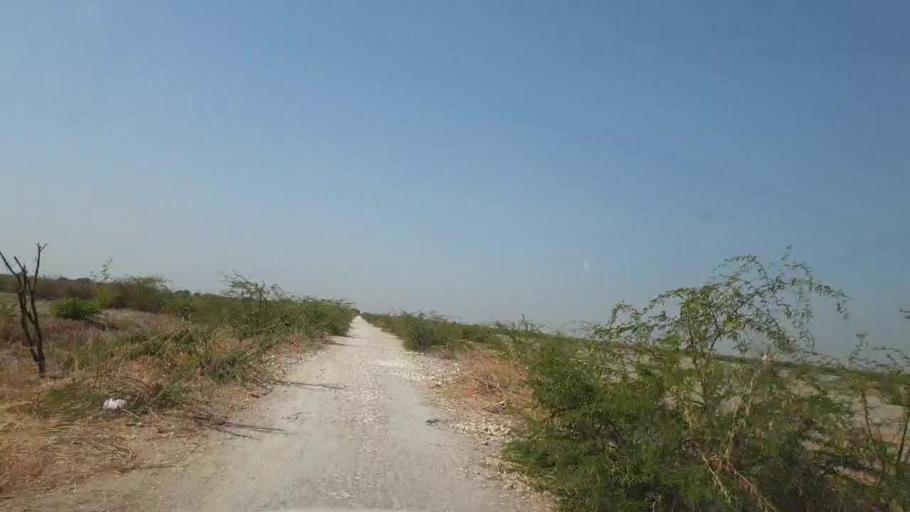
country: PK
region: Sindh
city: Kunri
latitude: 25.0965
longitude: 69.4780
